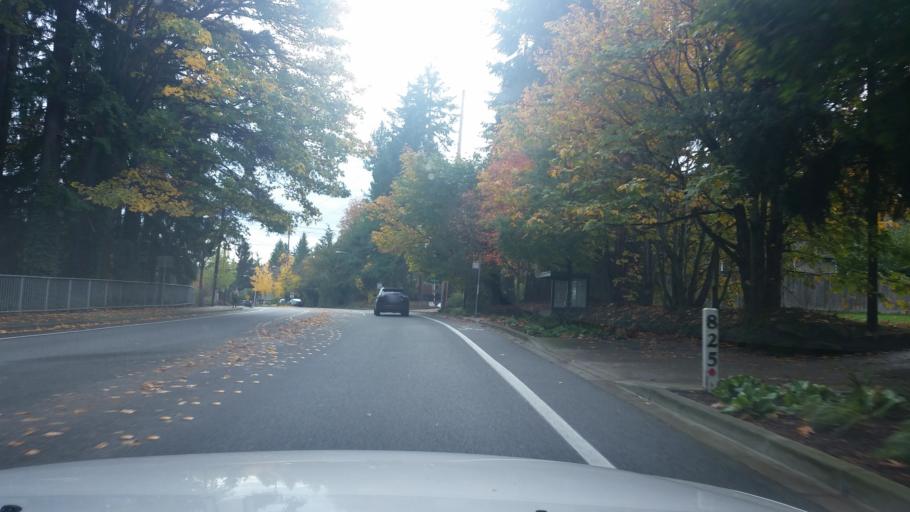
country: US
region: Washington
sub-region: King County
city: Eastgate
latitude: 47.6021
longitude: -122.1535
